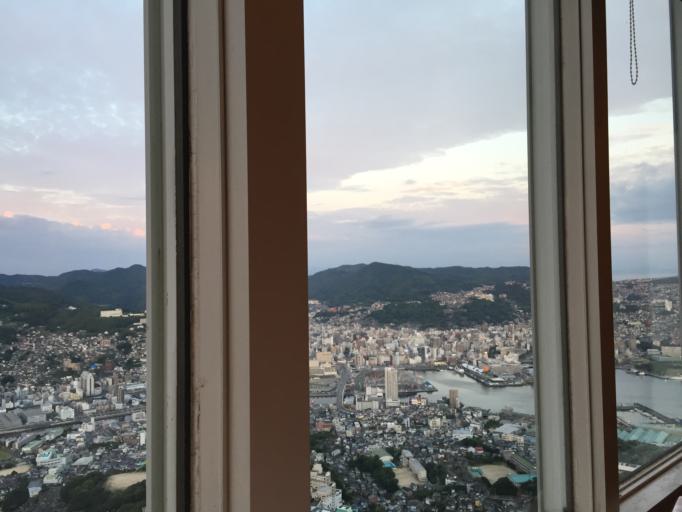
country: JP
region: Nagasaki
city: Nagasaki-shi
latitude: 32.7527
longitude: 129.8495
